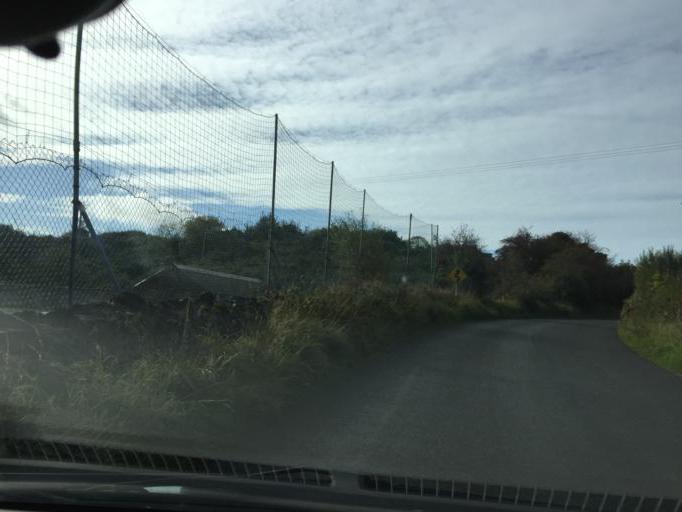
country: IE
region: Connaught
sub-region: Roscommon
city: Boyle
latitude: 54.0556
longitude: -8.2463
